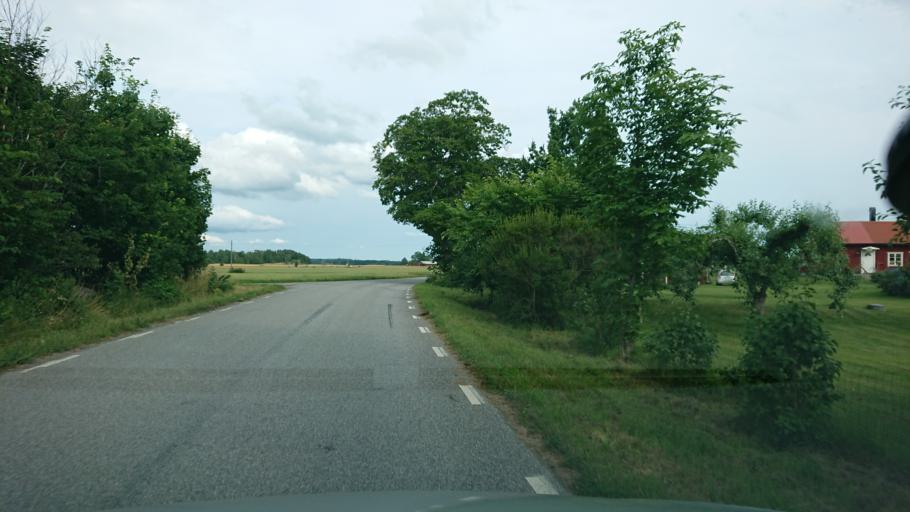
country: SE
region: Uppsala
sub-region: Osthammars Kommun
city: Bjorklinge
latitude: 59.9984
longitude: 17.4872
